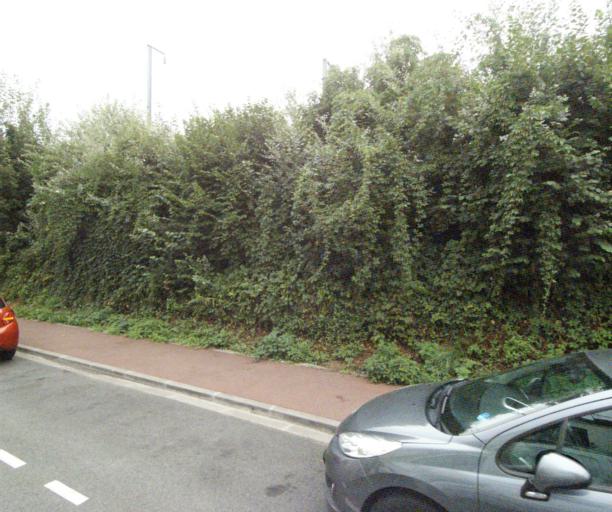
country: FR
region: Nord-Pas-de-Calais
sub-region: Departement du Nord
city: Wasquehal
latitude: 50.6686
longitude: 3.1243
